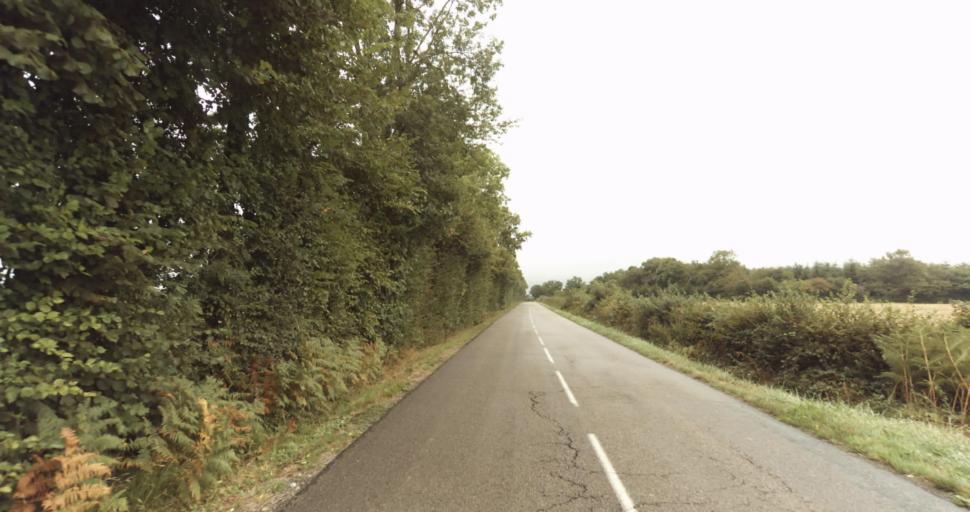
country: FR
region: Lower Normandy
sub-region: Departement de l'Orne
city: Vimoutiers
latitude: 48.8721
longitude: 0.1876
